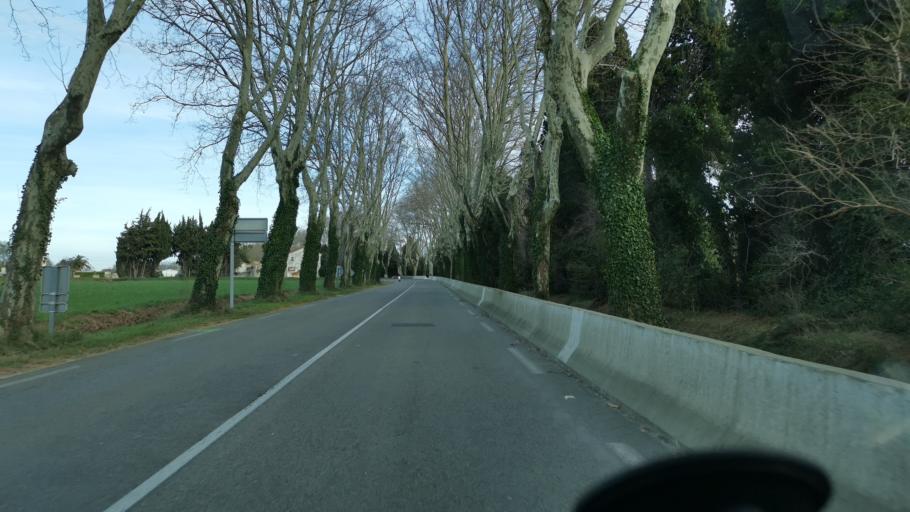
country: FR
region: Provence-Alpes-Cote d'Azur
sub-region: Departement des Bouches-du-Rhone
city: Saint-Martin-de-Crau
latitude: 43.6367
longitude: 4.7469
